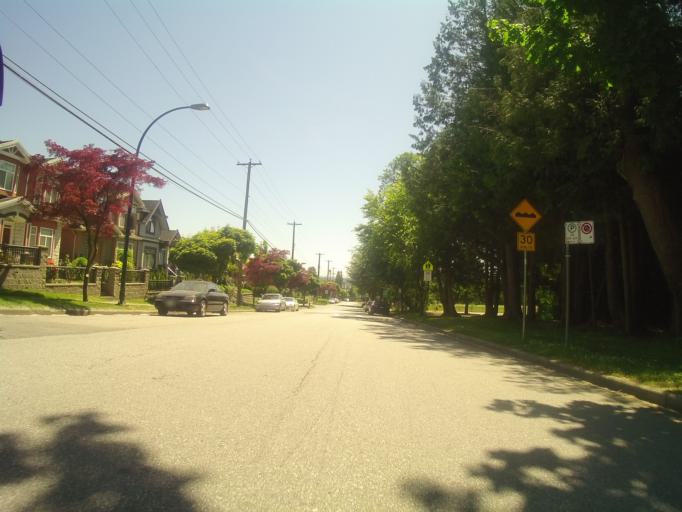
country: CA
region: British Columbia
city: Vancouver
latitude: 49.2186
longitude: -123.1062
